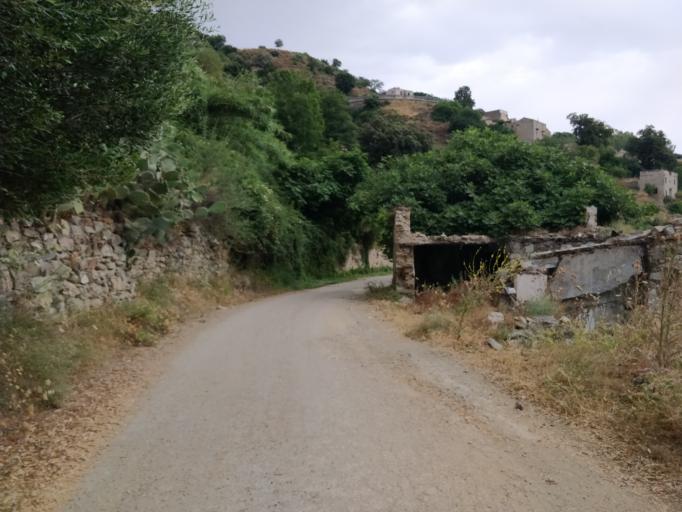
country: IT
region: Sardinia
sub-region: Provincia di Ogliastra
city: Gairo Sant'Elena
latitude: 39.8486
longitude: 9.4990
